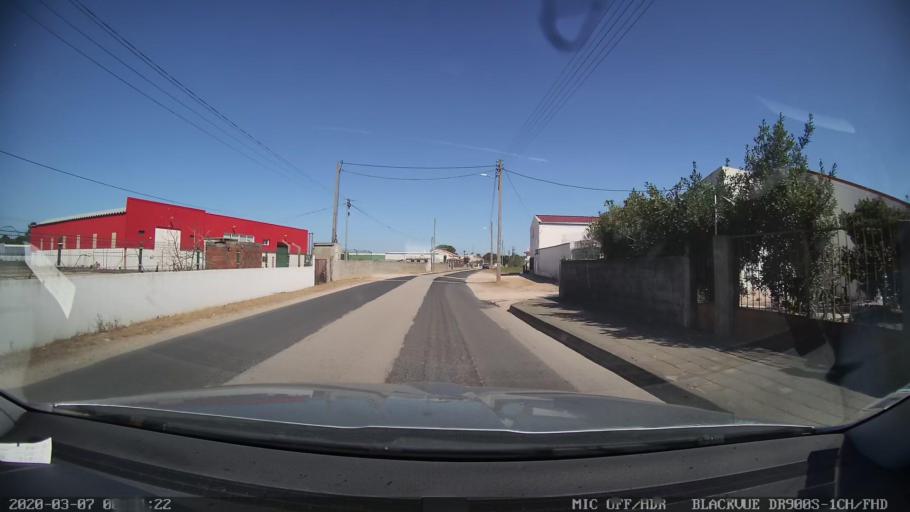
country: PT
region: Santarem
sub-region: Benavente
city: Benavente
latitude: 38.9509
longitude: -8.8201
